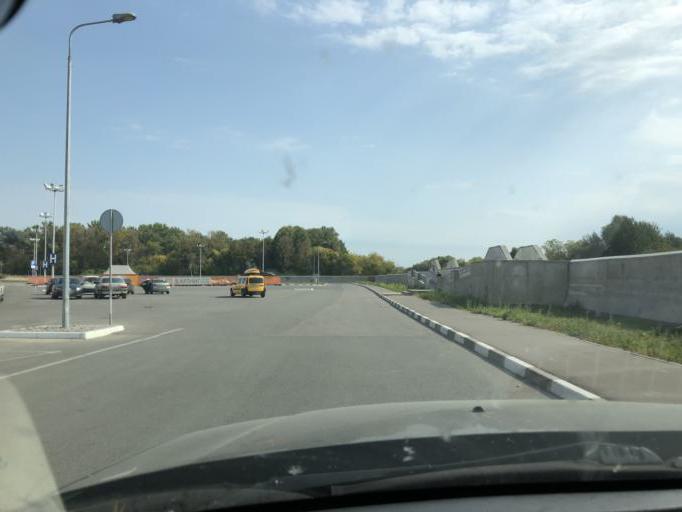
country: RU
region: Tula
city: Tula
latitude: 54.1915
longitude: 37.6396
